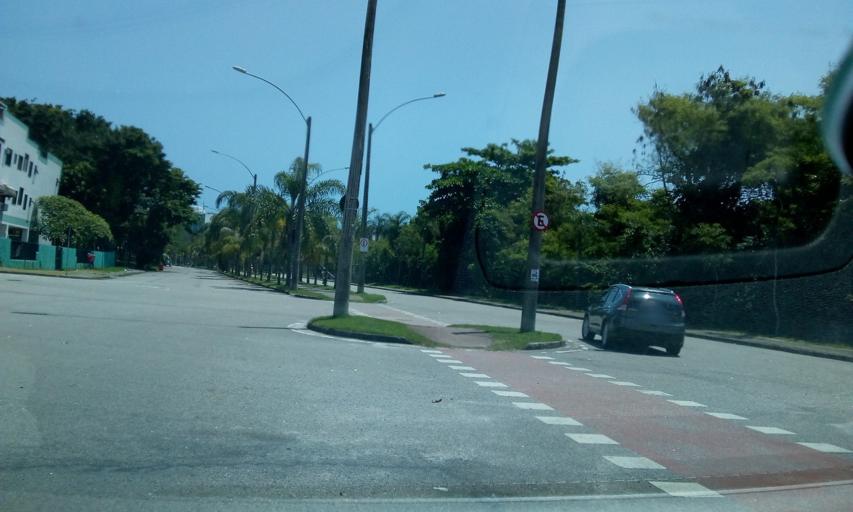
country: BR
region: Rio de Janeiro
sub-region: Nilopolis
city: Nilopolis
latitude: -23.0262
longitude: -43.4677
